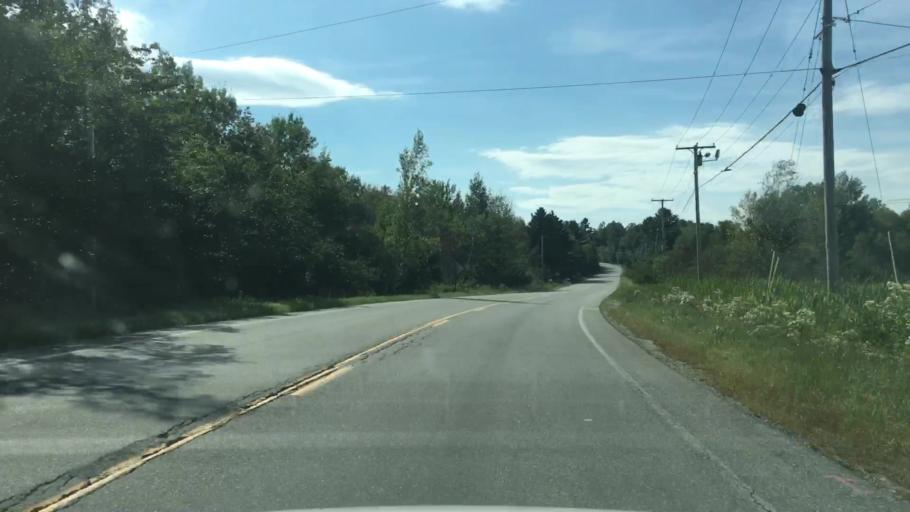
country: US
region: Maine
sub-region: Penobscot County
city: Lincoln
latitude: 45.3931
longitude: -68.5204
